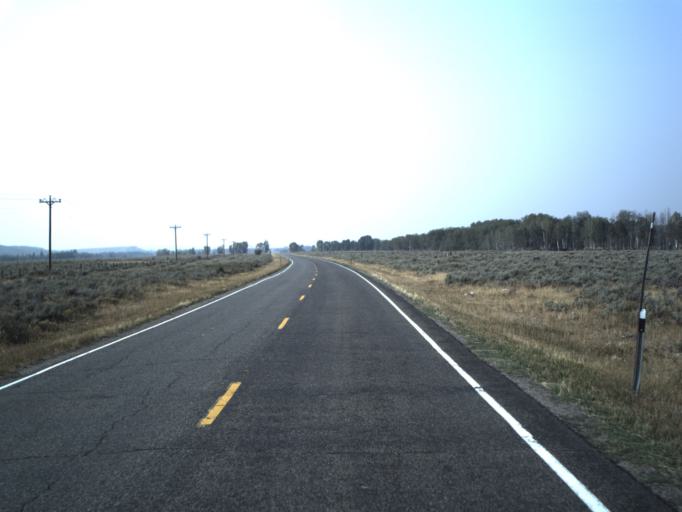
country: US
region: Wyoming
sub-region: Uinta County
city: Evanston
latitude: 40.9661
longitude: -110.8469
